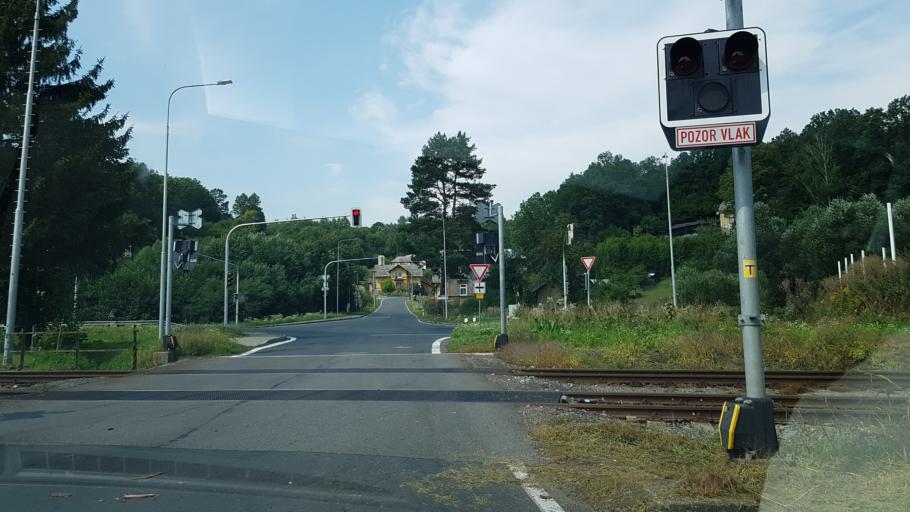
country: CZ
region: Olomoucky
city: Mikulovice
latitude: 50.3032
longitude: 17.3219
